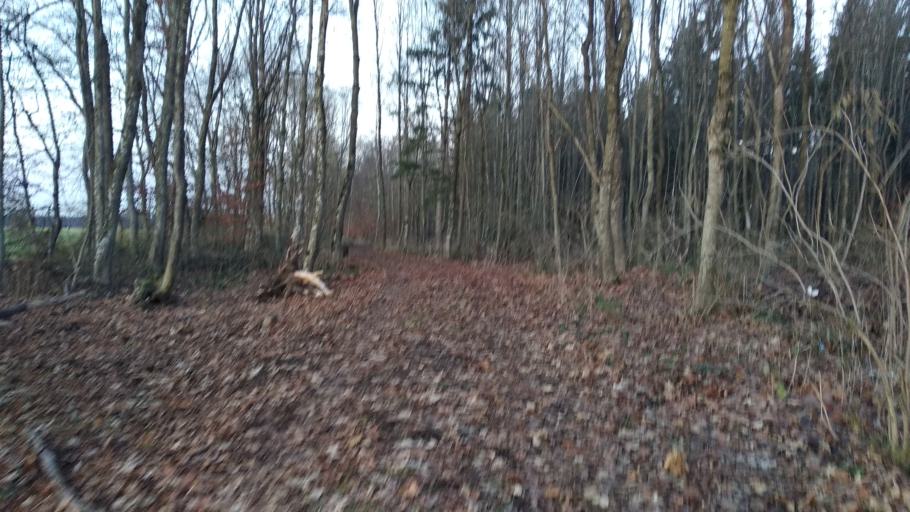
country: DE
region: Bavaria
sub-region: Upper Bavaria
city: Vaterstetten
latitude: 48.0695
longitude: 11.7851
